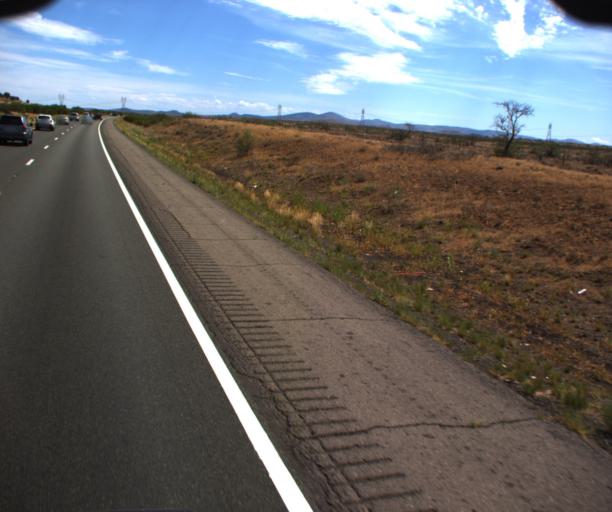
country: US
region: Arizona
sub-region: Yavapai County
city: Spring Valley
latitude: 34.3722
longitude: -112.1092
